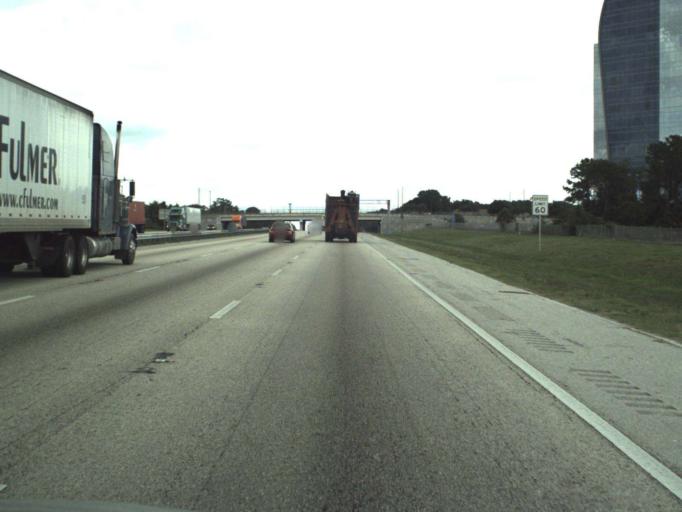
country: US
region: Florida
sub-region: Seminole County
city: Altamonte Springs
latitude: 28.6693
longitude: -81.3885
